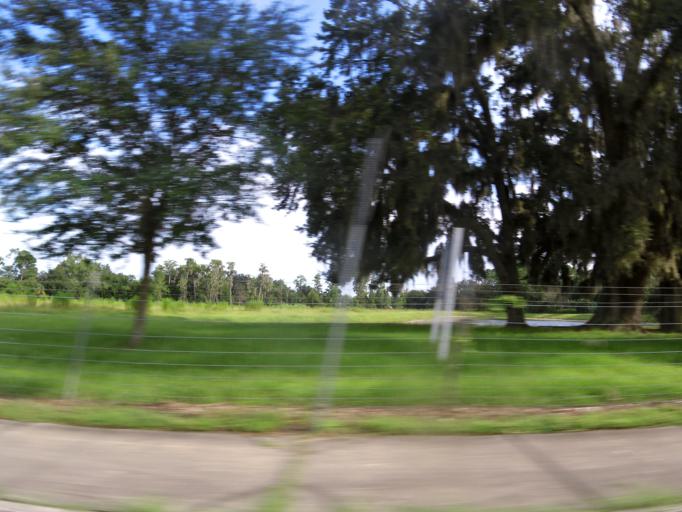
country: US
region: Florida
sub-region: Saint Johns County
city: Fruit Cove
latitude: 30.1860
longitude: -81.5972
